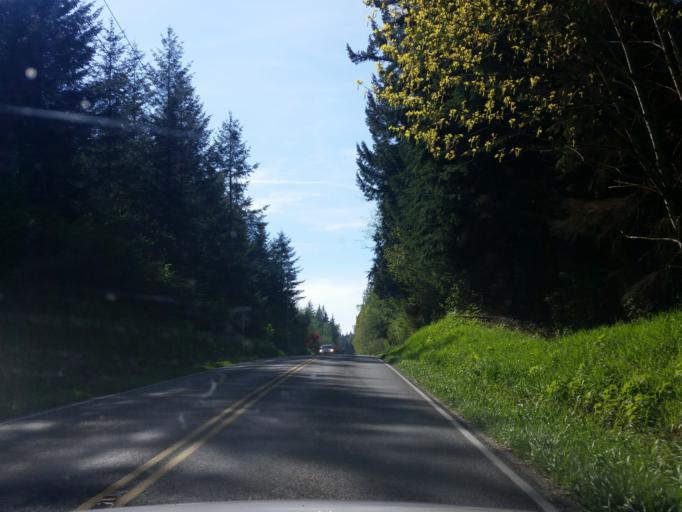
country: US
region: Washington
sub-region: Snohomish County
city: Three Lakes
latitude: 47.9631
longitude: -121.9824
